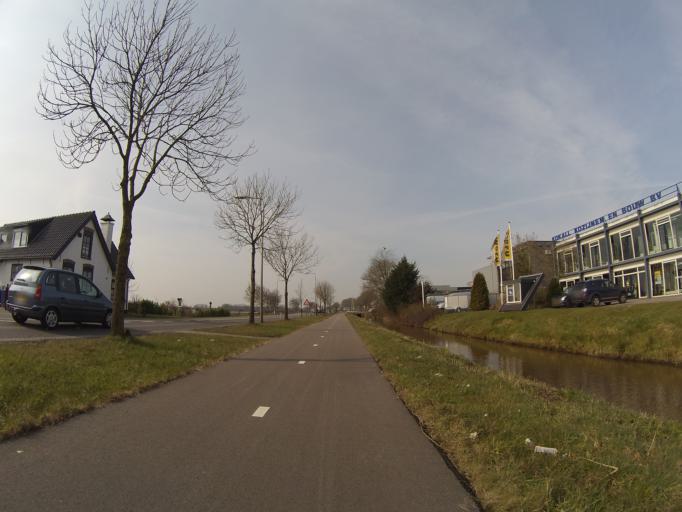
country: NL
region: Utrecht
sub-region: Gemeente Bunschoten
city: Bunschoten
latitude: 52.2277
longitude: 5.3659
